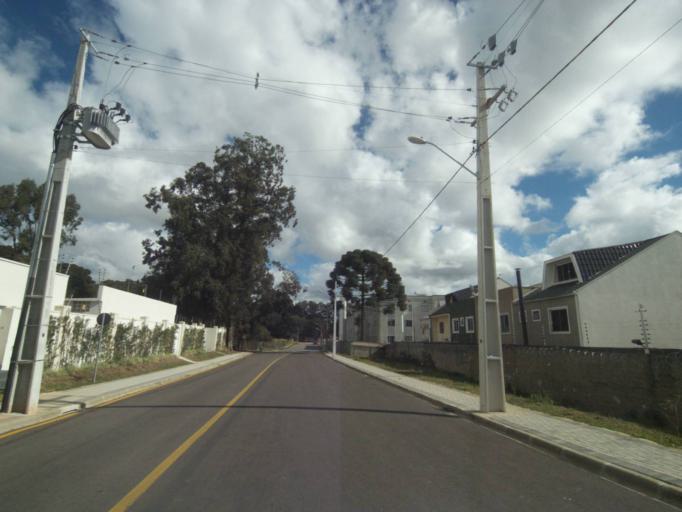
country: BR
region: Parana
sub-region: Sao Jose Dos Pinhais
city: Sao Jose dos Pinhais
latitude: -25.5301
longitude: -49.2930
